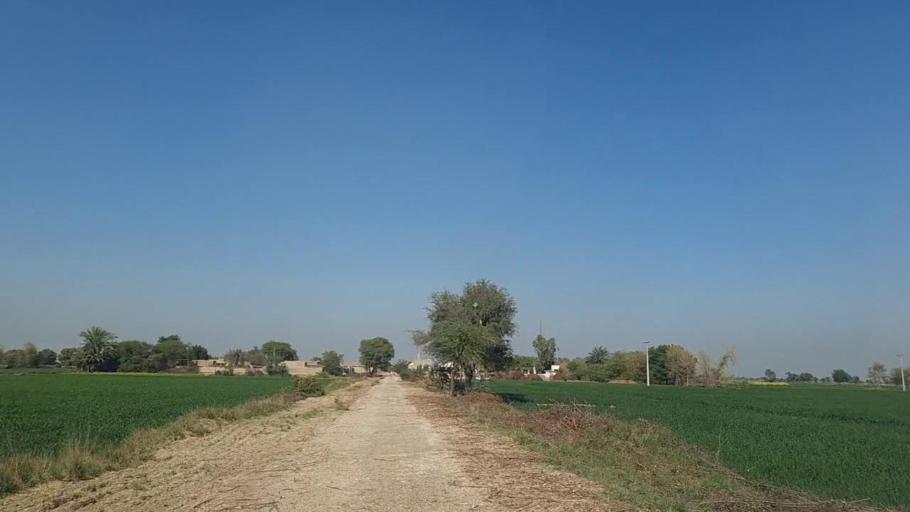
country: PK
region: Sindh
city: Shahpur Chakar
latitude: 26.2155
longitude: 68.5764
